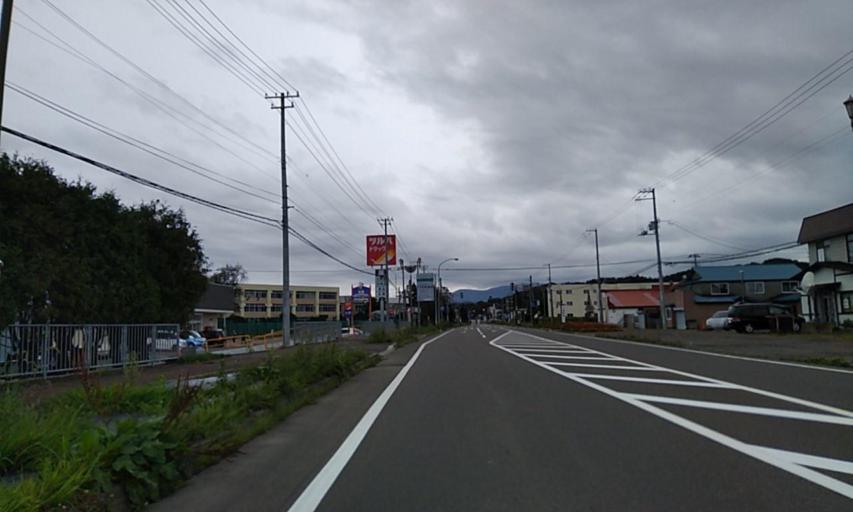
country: JP
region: Hokkaido
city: Obihiro
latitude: 42.2988
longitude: 143.3148
